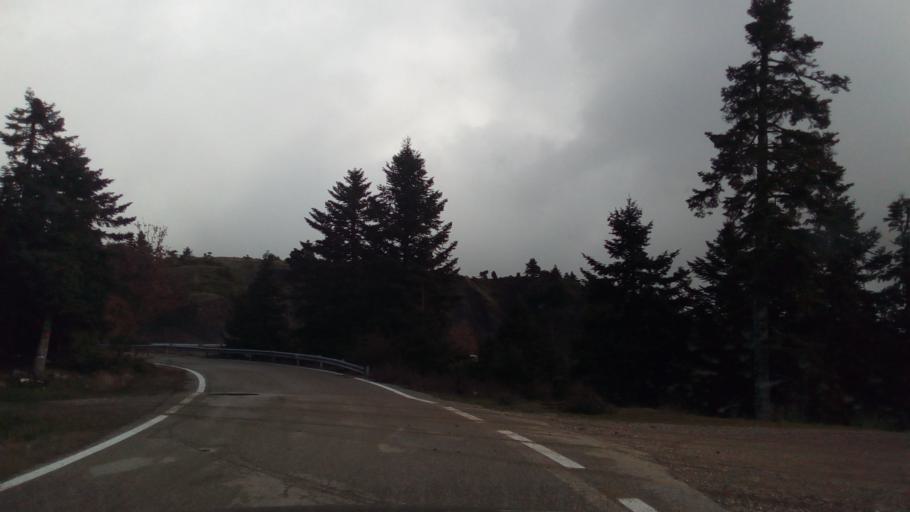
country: GR
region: West Greece
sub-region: Nomos Aitolias kai Akarnanias
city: Nafpaktos
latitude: 38.5865
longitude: 21.9576
